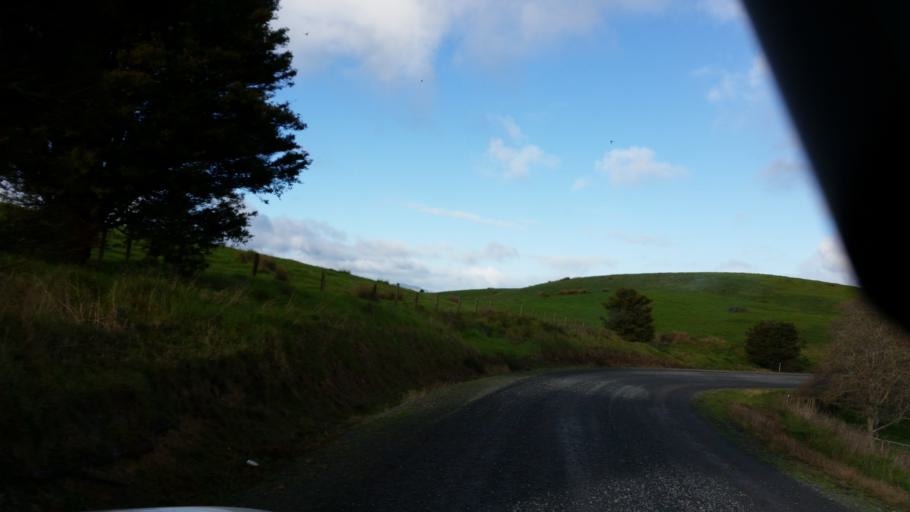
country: NZ
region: Northland
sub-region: Whangarei
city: Maungatapere
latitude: -35.7017
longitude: 174.0930
